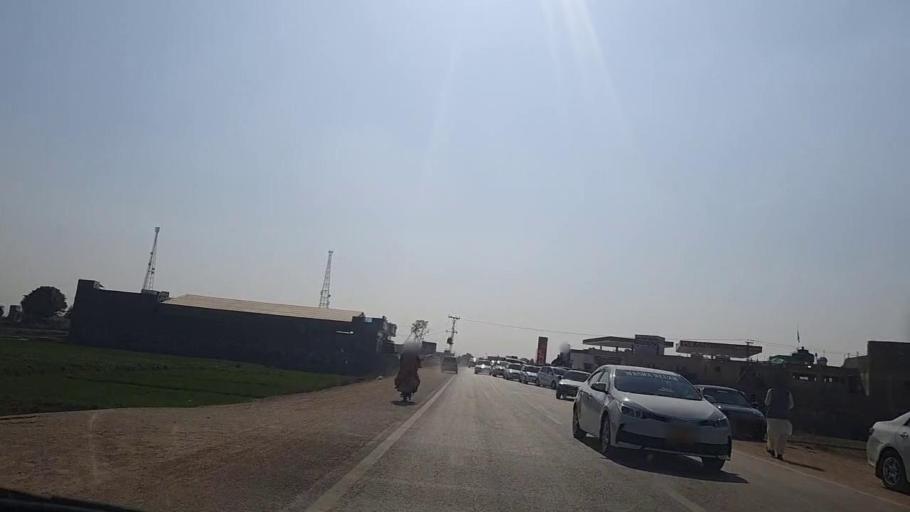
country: PK
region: Sindh
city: Hala
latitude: 25.9757
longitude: 68.3810
